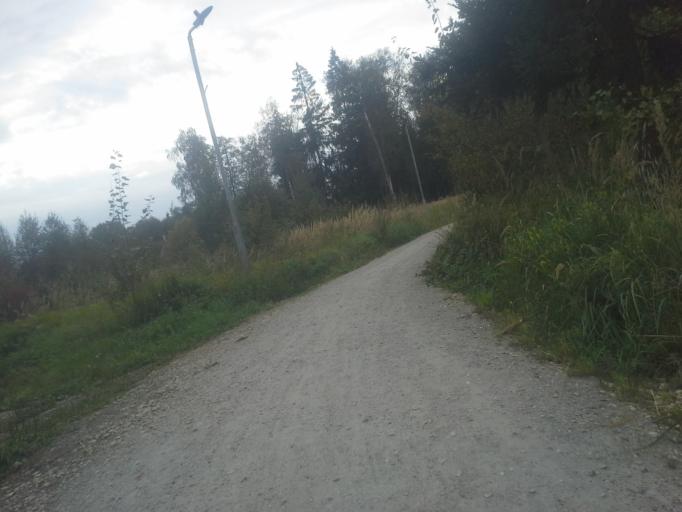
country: RU
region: Moskovskaya
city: Kievskij
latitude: 55.4251
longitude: 36.8829
